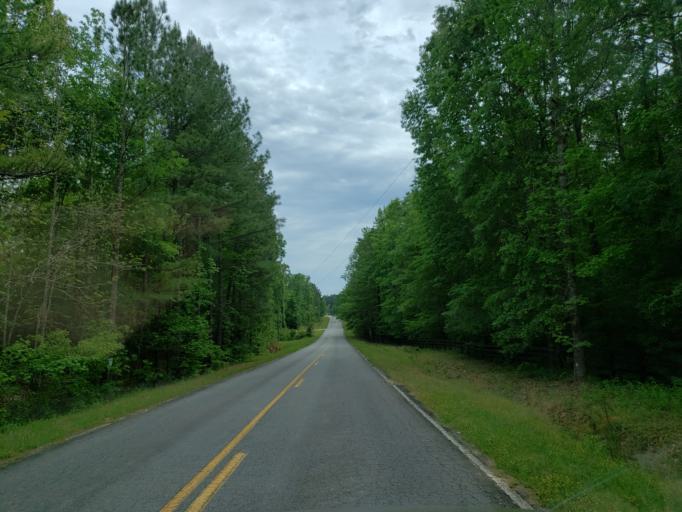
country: US
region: Georgia
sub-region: Bibb County
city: West Point
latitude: 32.8471
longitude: -83.8891
